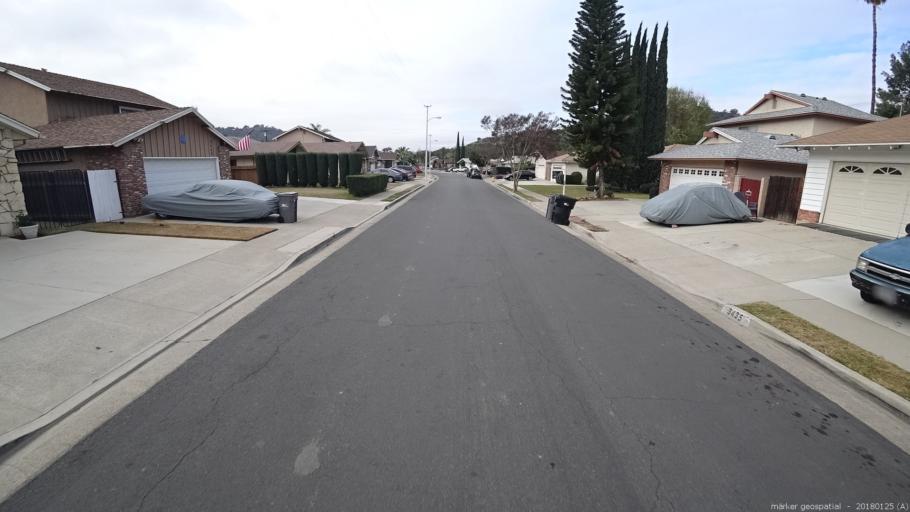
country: US
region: California
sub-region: Los Angeles County
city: Walnut
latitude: 33.9661
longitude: -117.8488
